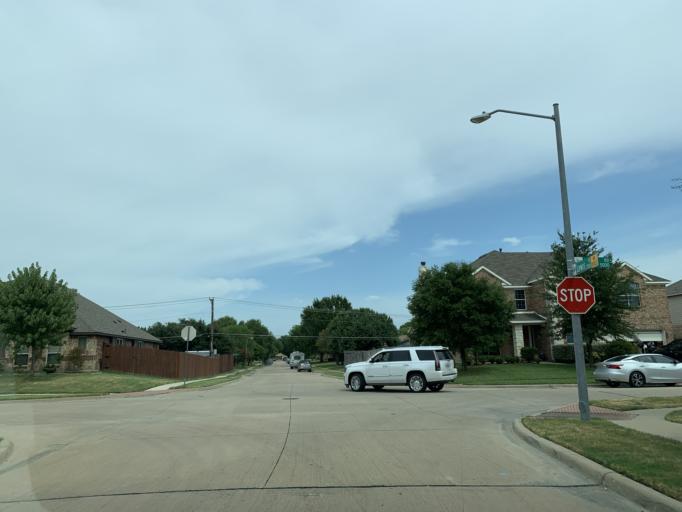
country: US
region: Texas
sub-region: Dallas County
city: Cedar Hill
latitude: 32.6500
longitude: -97.0358
